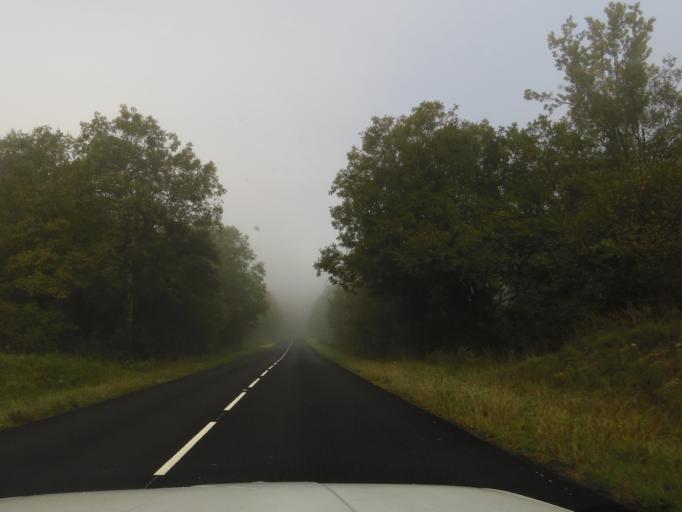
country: FR
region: Rhone-Alpes
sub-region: Departement de l'Isere
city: Creys-Mepieu
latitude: 45.7518
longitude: 5.5015
